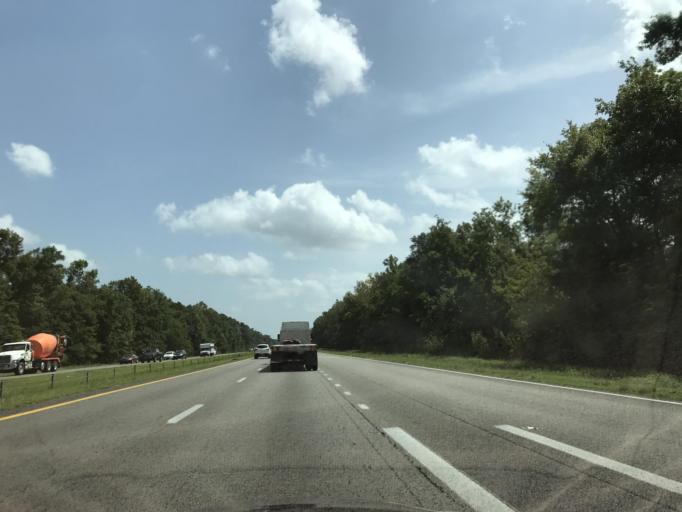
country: US
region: North Carolina
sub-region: Pender County
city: Rocky Point
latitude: 34.4369
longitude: -77.8733
